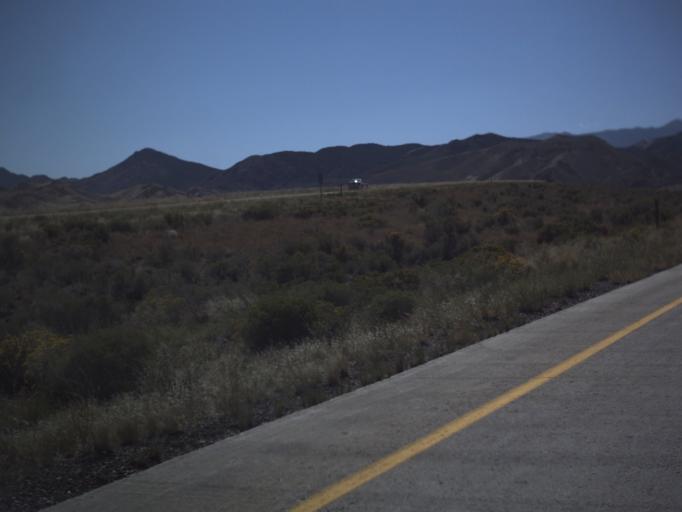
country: US
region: Utah
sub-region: Sevier County
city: Monroe
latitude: 38.6291
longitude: -112.2254
